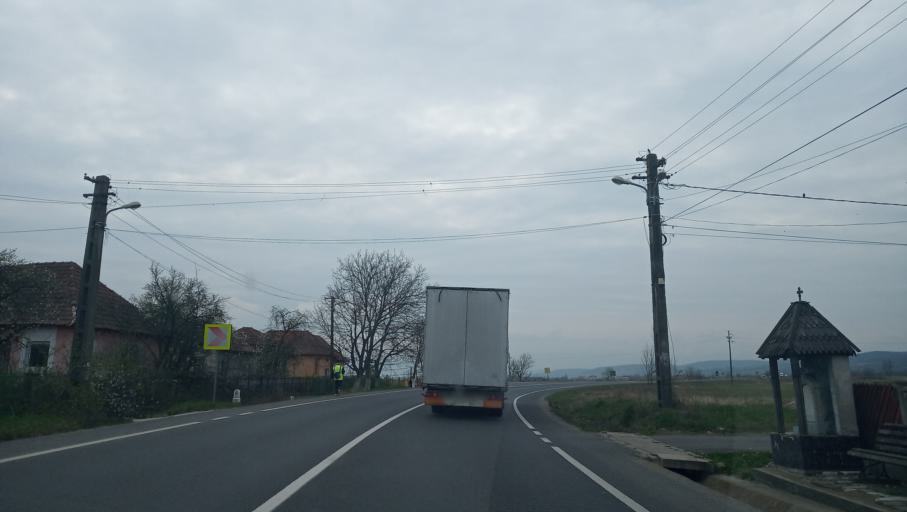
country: RO
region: Hunedoara
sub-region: Comuna Calan
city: Calan
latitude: 45.7135
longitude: 22.9930
